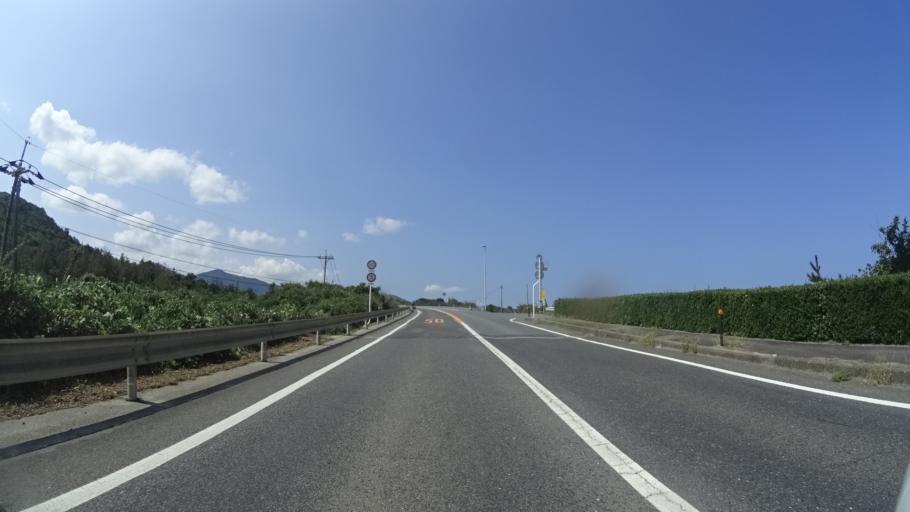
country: JP
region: Shimane
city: Masuda
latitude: 34.6771
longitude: 131.7571
